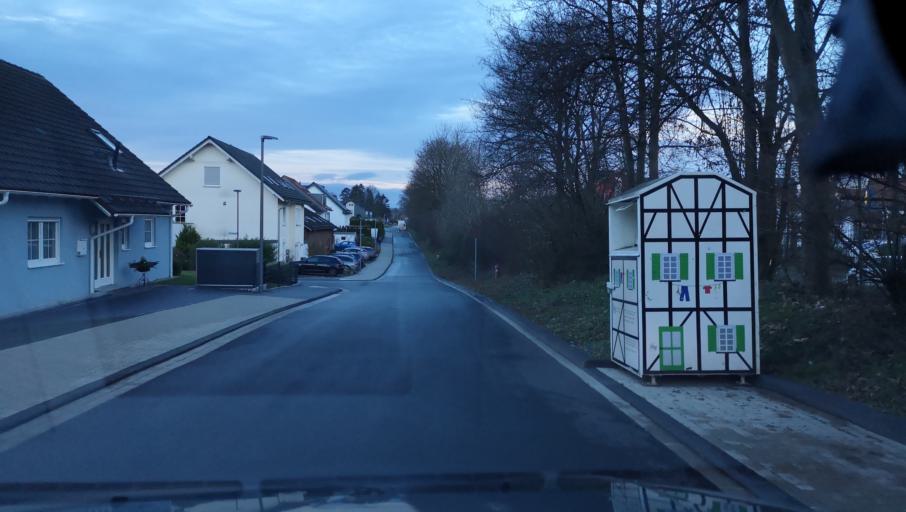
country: DE
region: North Rhine-Westphalia
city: Radevormwald
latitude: 51.2007
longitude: 7.3639
